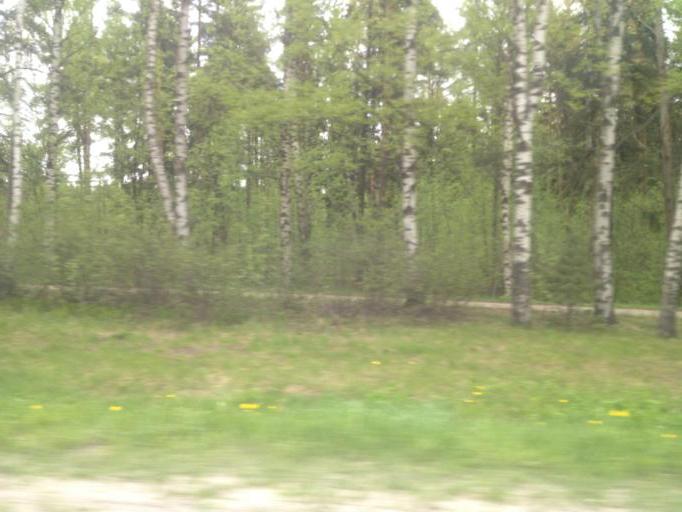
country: FI
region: Uusimaa
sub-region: Helsinki
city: Helsinki
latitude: 60.2310
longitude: 24.9040
